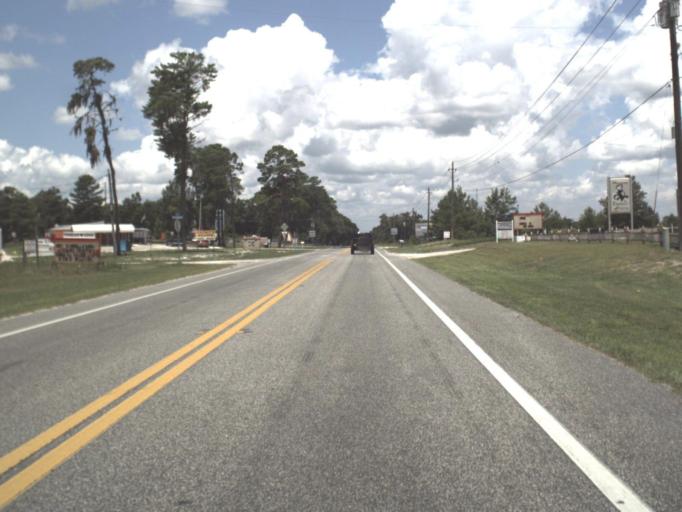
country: US
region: Florida
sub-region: Putnam County
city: Crescent City
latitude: 29.4844
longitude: -81.5632
